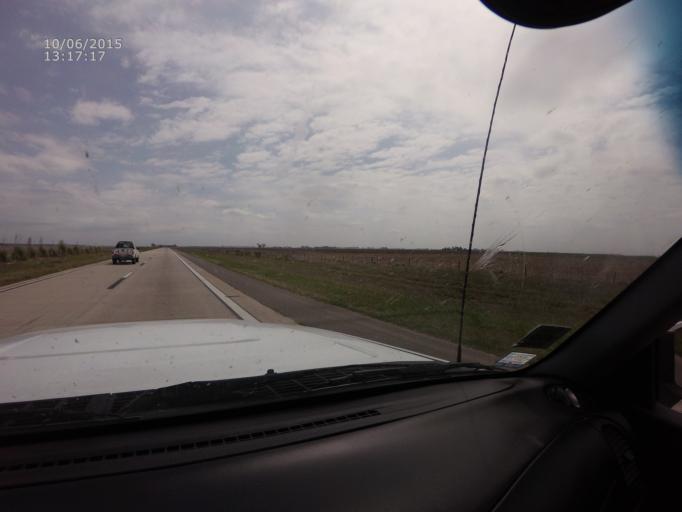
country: AR
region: Cordoba
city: General Roca
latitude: -32.6891
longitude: -61.9894
